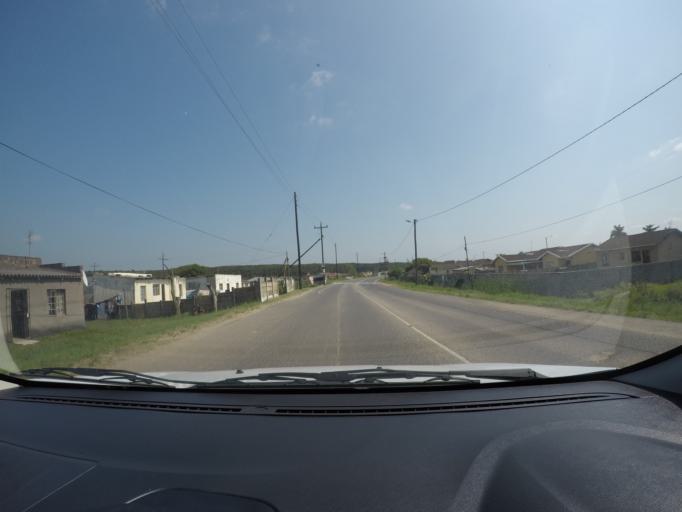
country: ZA
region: KwaZulu-Natal
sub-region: uThungulu District Municipality
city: eSikhawini
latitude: -28.8915
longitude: 31.8809
